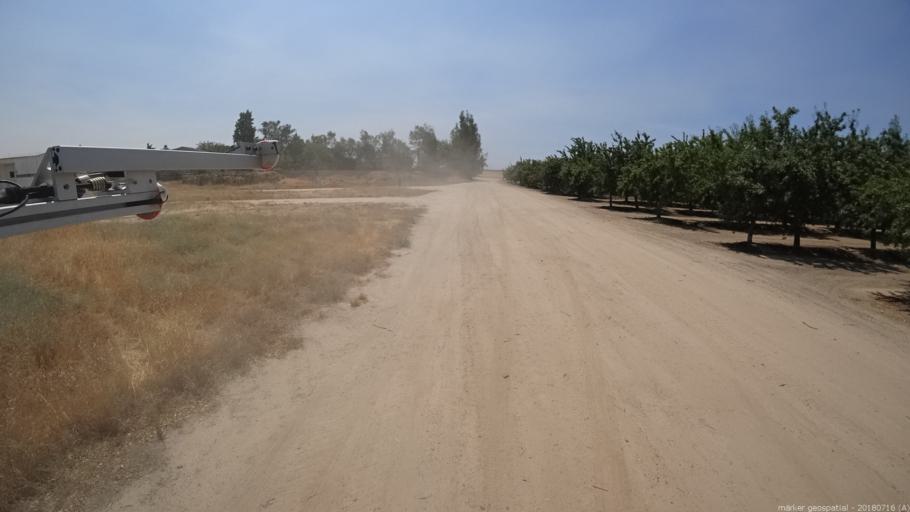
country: US
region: California
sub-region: Madera County
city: Madera Acres
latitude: 37.0543
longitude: -120.0925
